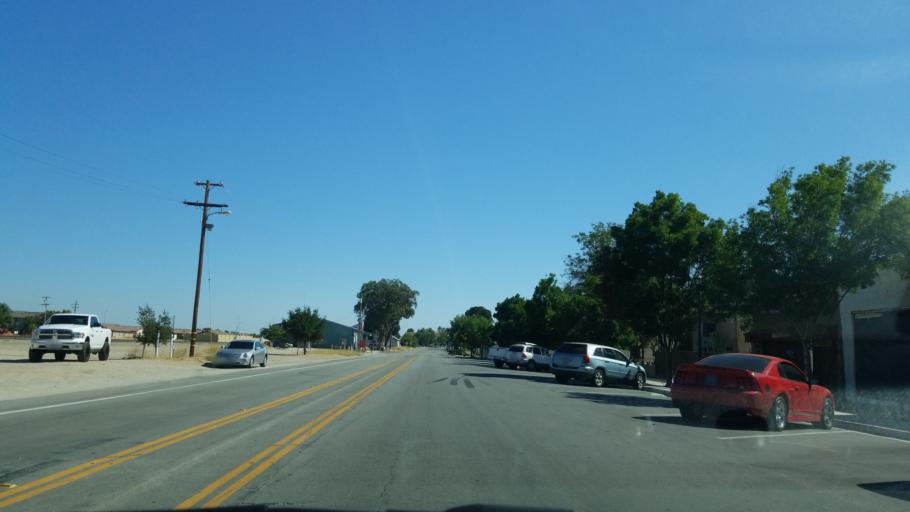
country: US
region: California
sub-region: San Luis Obispo County
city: San Miguel
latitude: 35.7512
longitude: -120.6964
